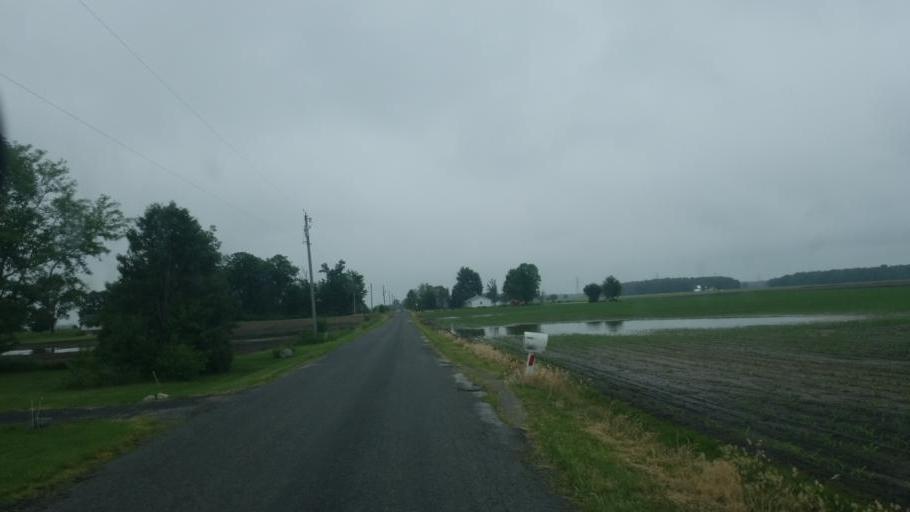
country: US
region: Indiana
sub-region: Marshall County
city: Bremen
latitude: 41.4793
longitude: -86.1400
